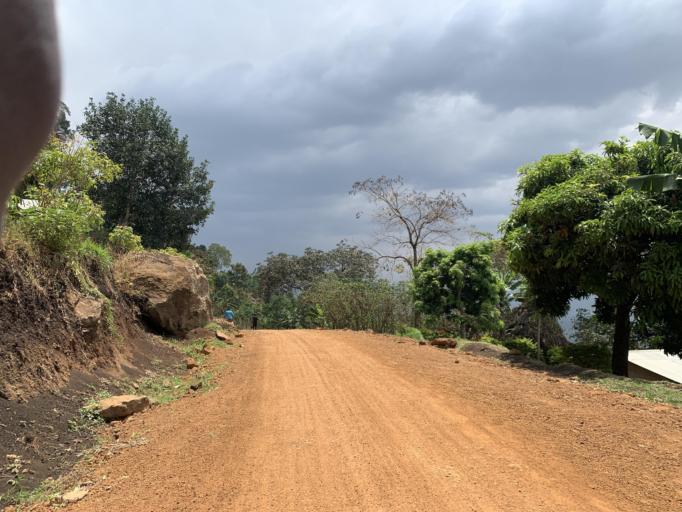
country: UG
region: Eastern Region
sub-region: Sironko District
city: Sironko
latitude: 1.2610
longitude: 34.2979
